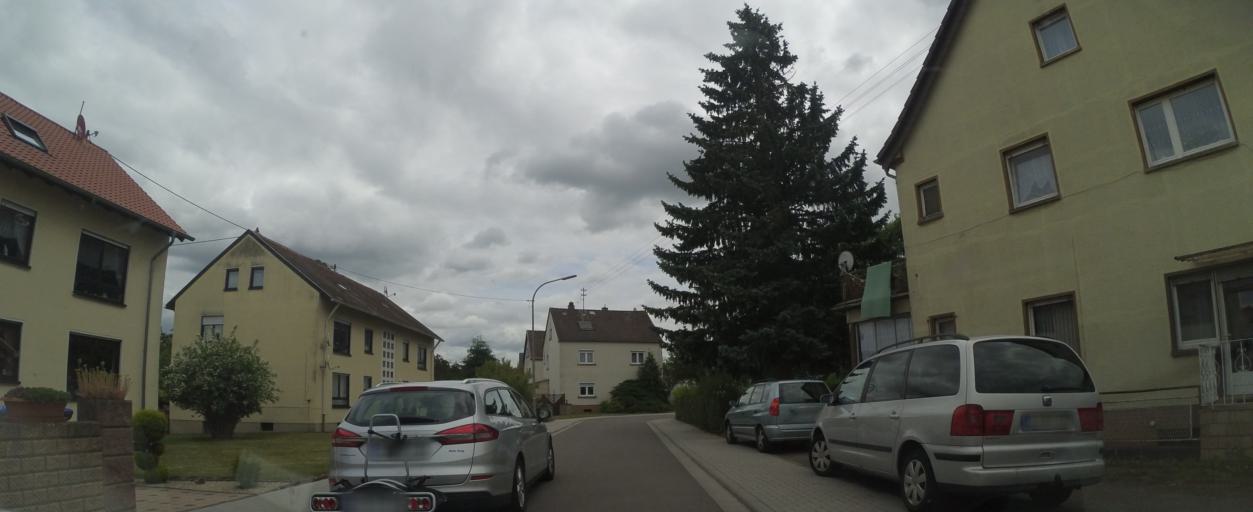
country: DE
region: Saarland
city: Lebach
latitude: 49.4070
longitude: 6.9014
